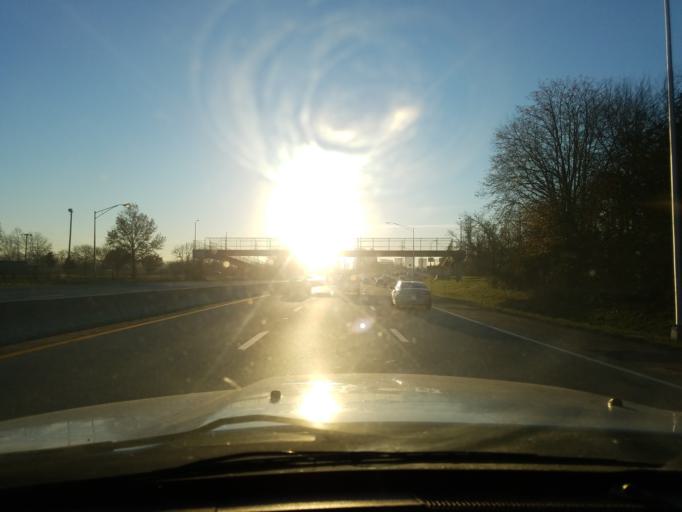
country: US
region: Kentucky
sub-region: Jefferson County
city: Louisville
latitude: 38.2732
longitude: -85.7859
